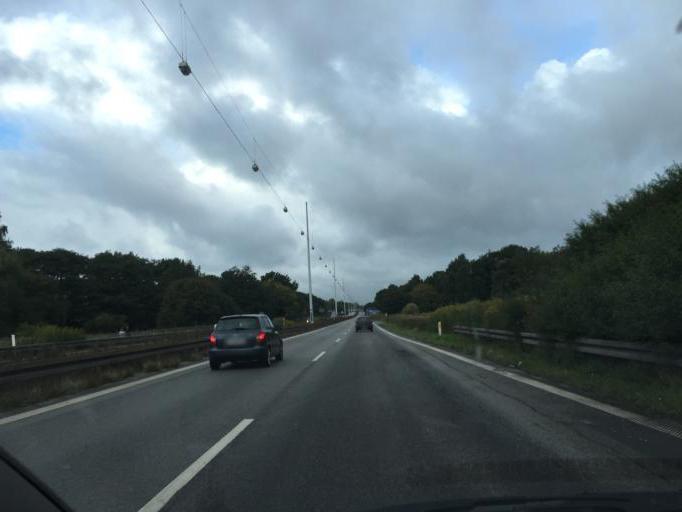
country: DK
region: Capital Region
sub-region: Gladsaxe Municipality
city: Buddinge
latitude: 55.7259
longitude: 12.4850
